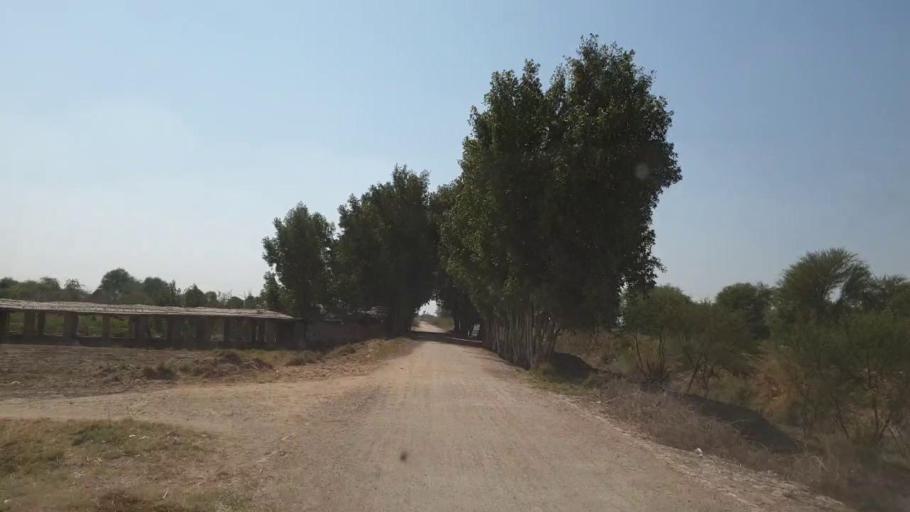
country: PK
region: Sindh
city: Mirpur Khas
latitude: 25.7187
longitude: 69.1036
